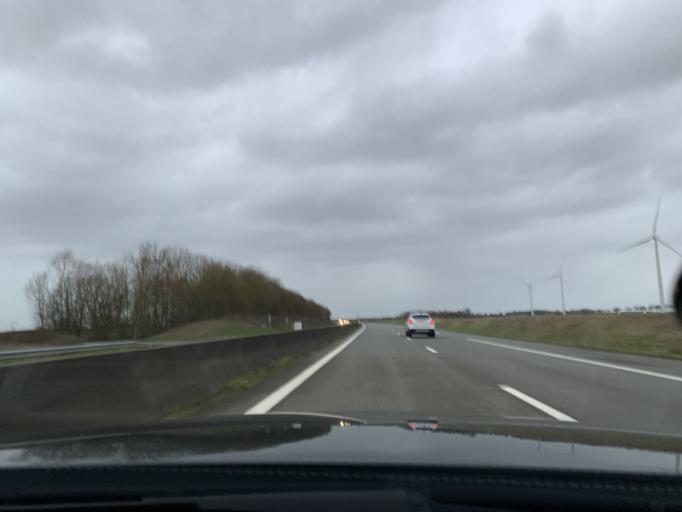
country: FR
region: Picardie
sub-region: Departement de la Somme
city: Conty
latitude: 49.7101
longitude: 2.2394
